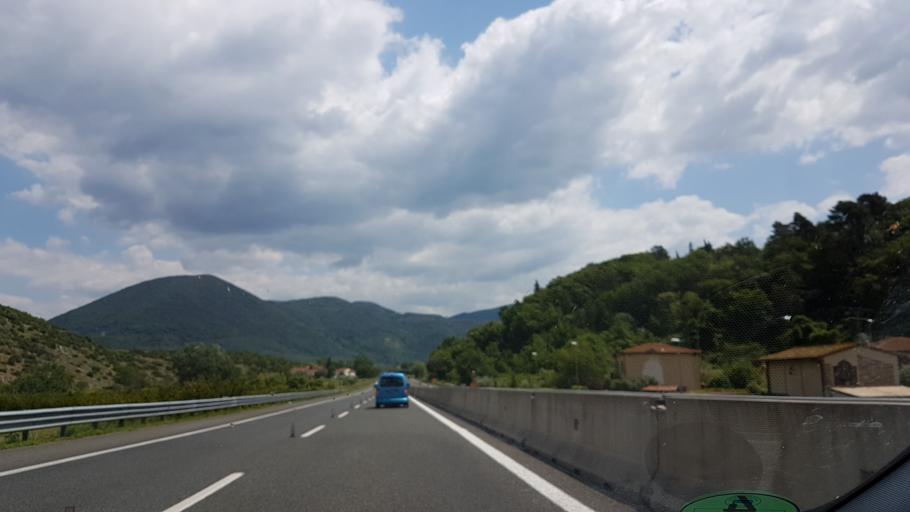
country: IT
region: Tuscany
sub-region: Province of Pisa
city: Filettole
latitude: 43.8075
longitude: 10.3868
